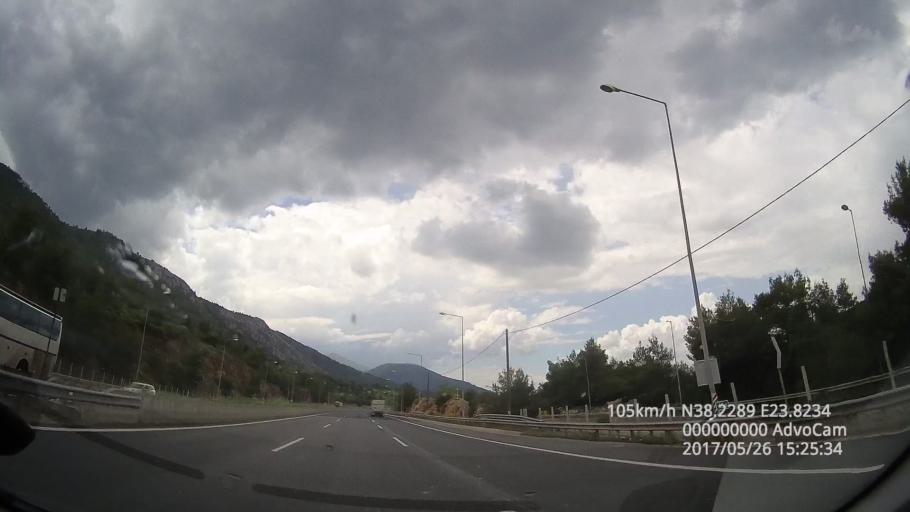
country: GR
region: Central Greece
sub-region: Nomos Voiotias
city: Akraifnia
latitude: 38.4583
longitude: 23.1644
